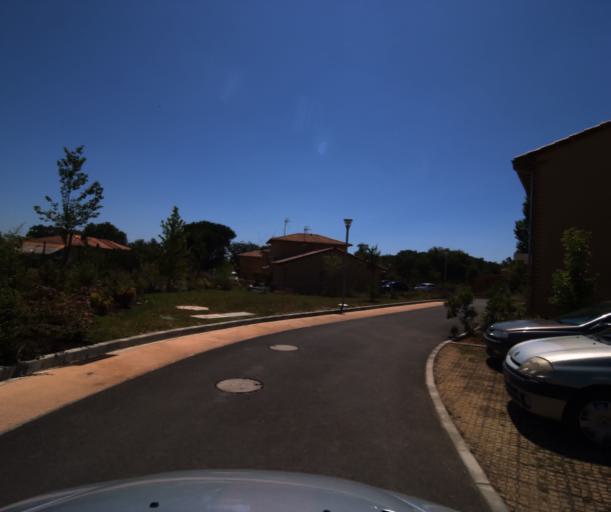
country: FR
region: Midi-Pyrenees
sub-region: Departement de la Haute-Garonne
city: Muret
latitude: 43.4537
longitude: 1.3403
